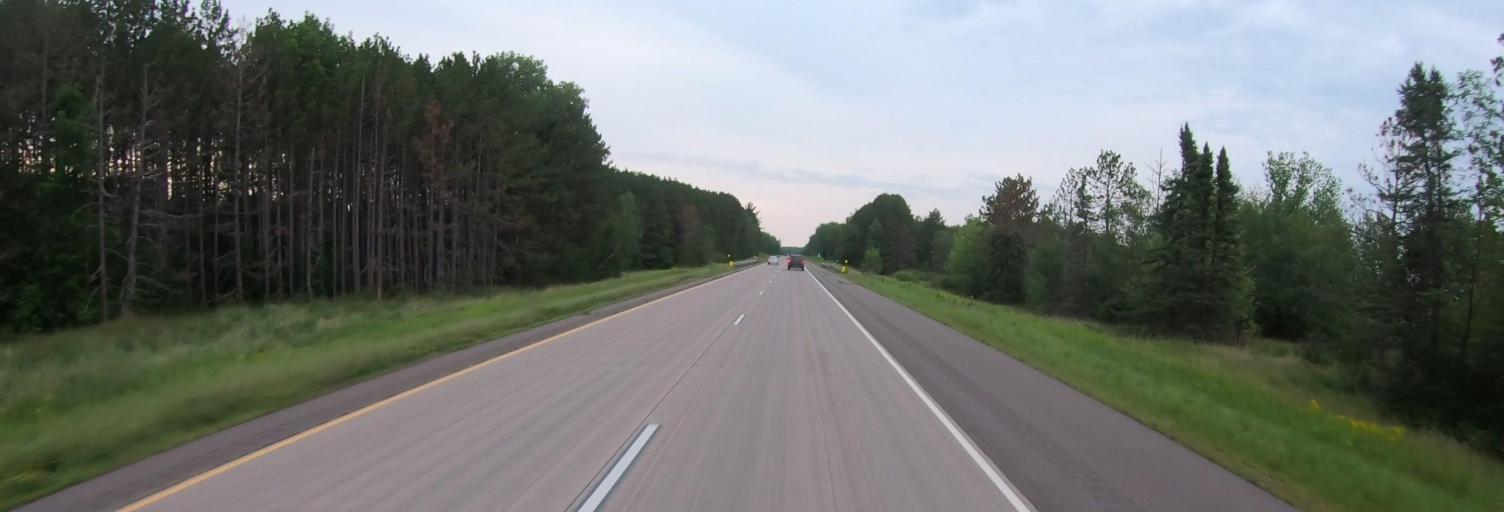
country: US
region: Minnesota
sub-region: Pine County
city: Sandstone
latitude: 46.0897
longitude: -92.8941
